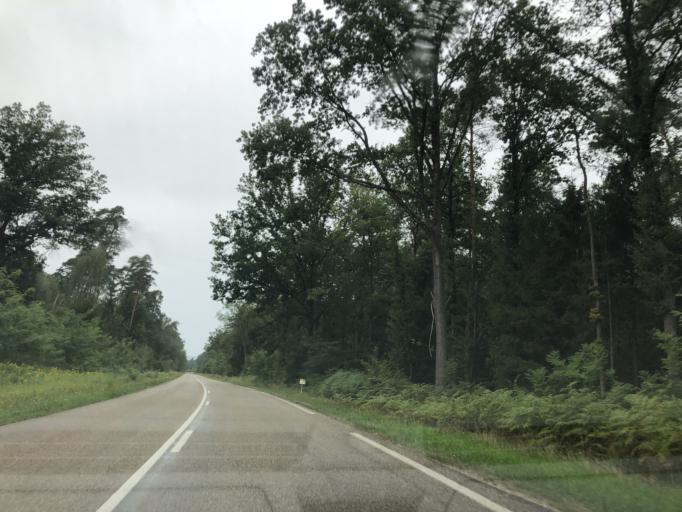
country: DE
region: Rheinland-Pfalz
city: Steinfeld
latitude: 49.0018
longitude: 8.0615
